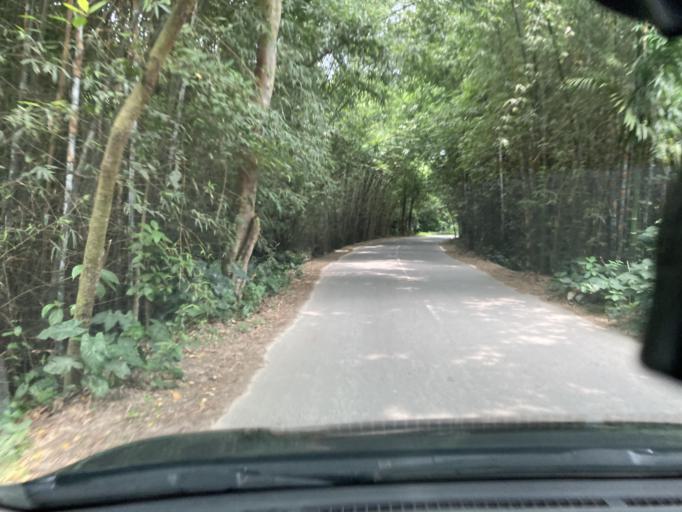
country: BD
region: Dhaka
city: Dohar
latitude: 23.7914
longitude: 90.0591
